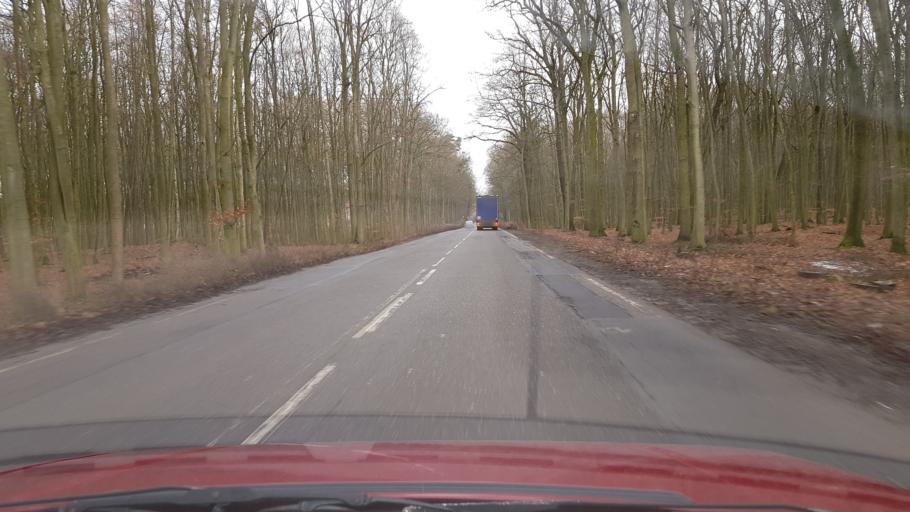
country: PL
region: West Pomeranian Voivodeship
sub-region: Powiat policki
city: Police
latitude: 53.5311
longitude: 14.5743
